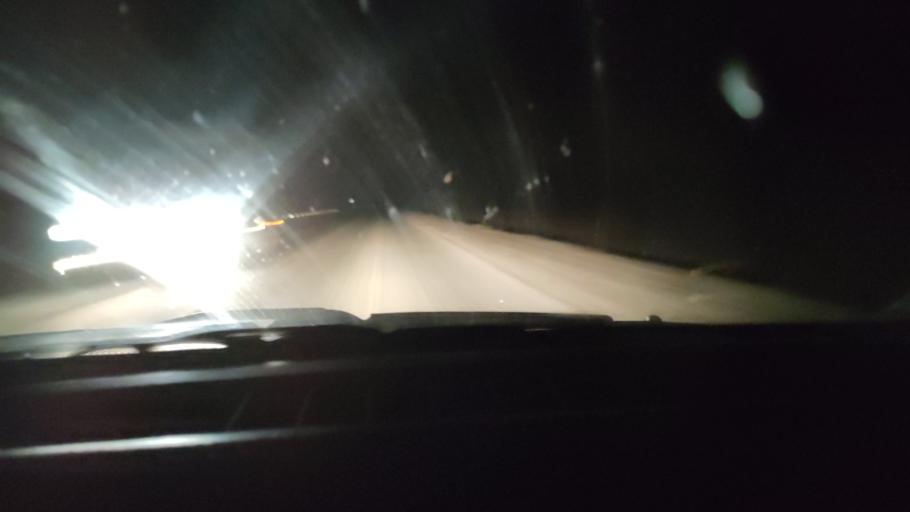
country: RU
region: Saratov
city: Dukhovnitskoye
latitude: 52.6766
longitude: 48.2280
